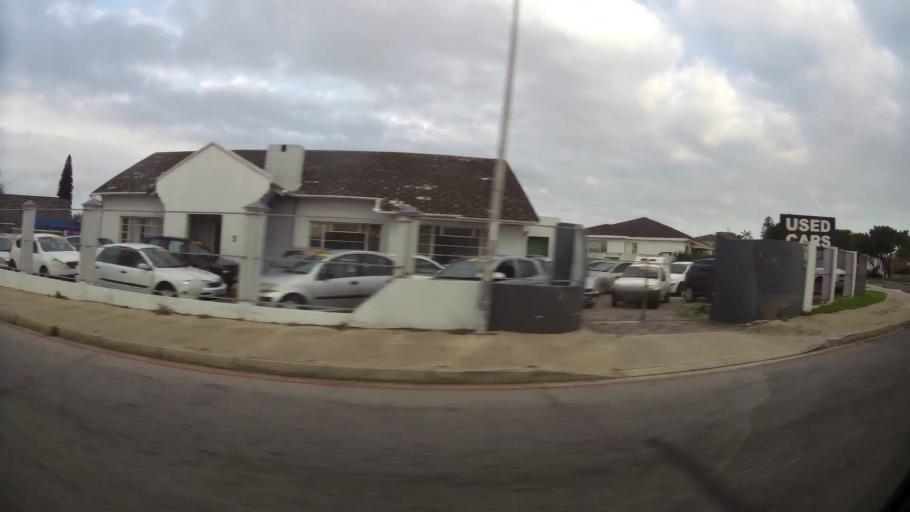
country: ZA
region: Eastern Cape
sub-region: Nelson Mandela Bay Metropolitan Municipality
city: Port Elizabeth
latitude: -33.9464
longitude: 25.5546
